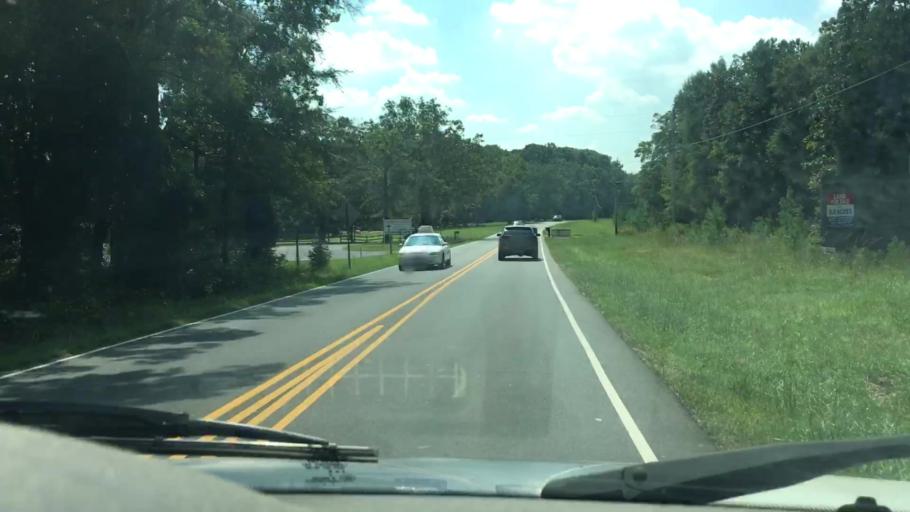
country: US
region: North Carolina
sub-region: Mecklenburg County
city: Huntersville
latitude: 35.3738
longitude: -80.8545
